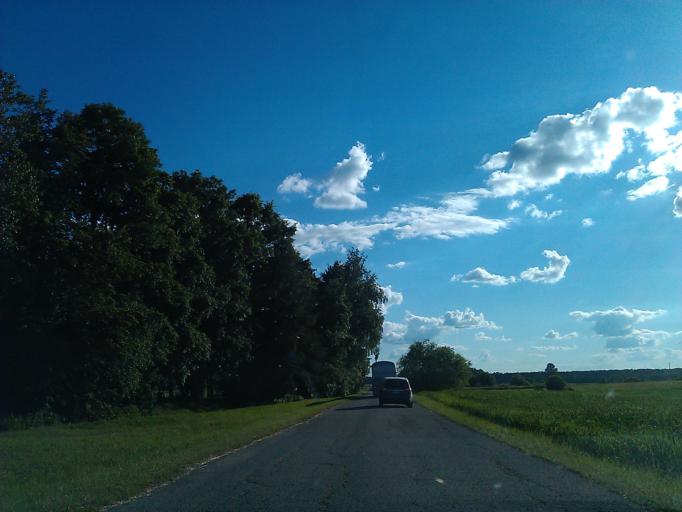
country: LV
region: Varaklani
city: Varaklani
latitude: 56.5782
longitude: 26.7966
